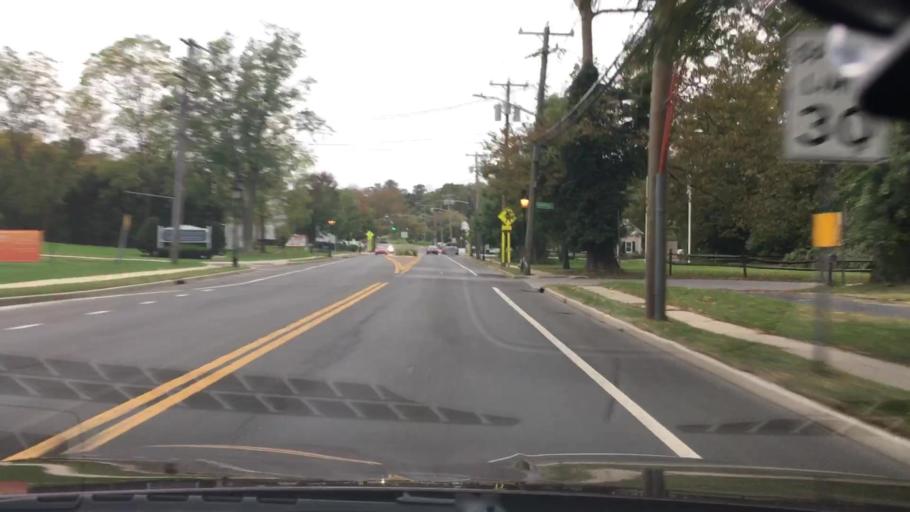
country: US
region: New York
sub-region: Suffolk County
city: East Setauket
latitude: 40.9437
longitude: -73.0991
